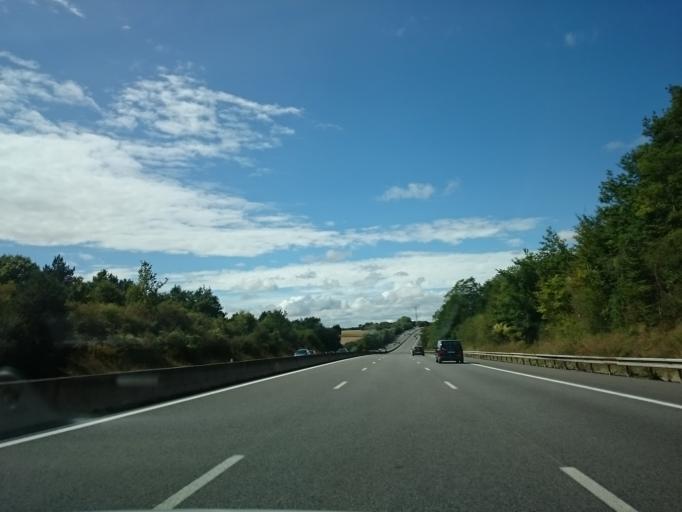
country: FR
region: Ile-de-France
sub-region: Departement des Yvelines
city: Ablis
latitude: 48.5179
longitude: 1.7917
